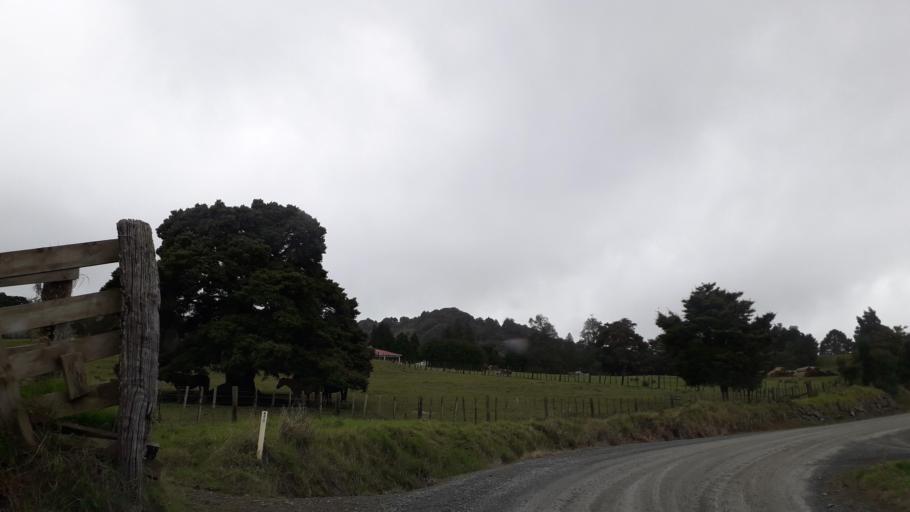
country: NZ
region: Northland
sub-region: Far North District
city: Kerikeri
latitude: -35.1269
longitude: 173.7443
